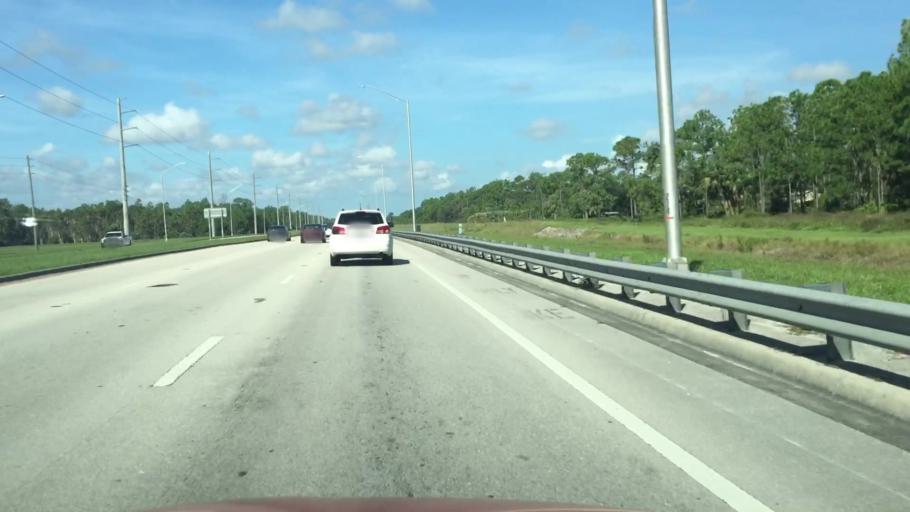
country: US
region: Florida
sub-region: Collier County
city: Orangetree
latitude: 26.2765
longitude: -81.6088
